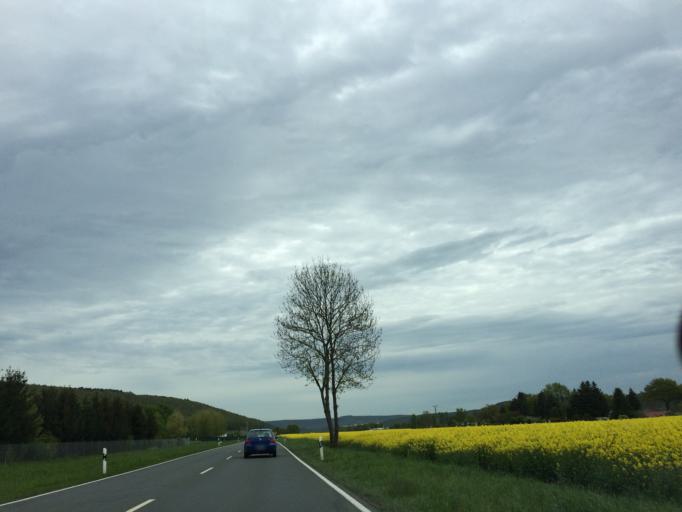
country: DE
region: Thuringia
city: Kahla
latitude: 50.8175
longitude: 11.5812
